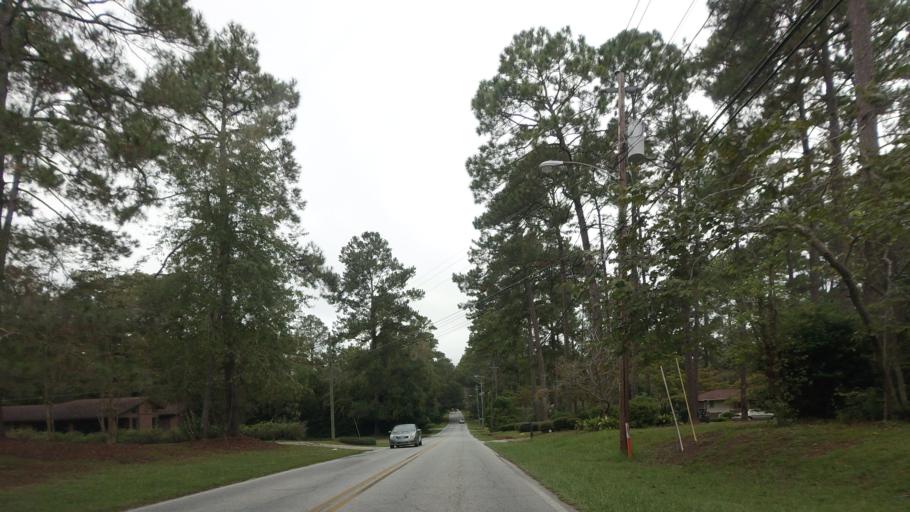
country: US
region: Georgia
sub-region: Lowndes County
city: Remerton
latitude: 30.8596
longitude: -83.2959
